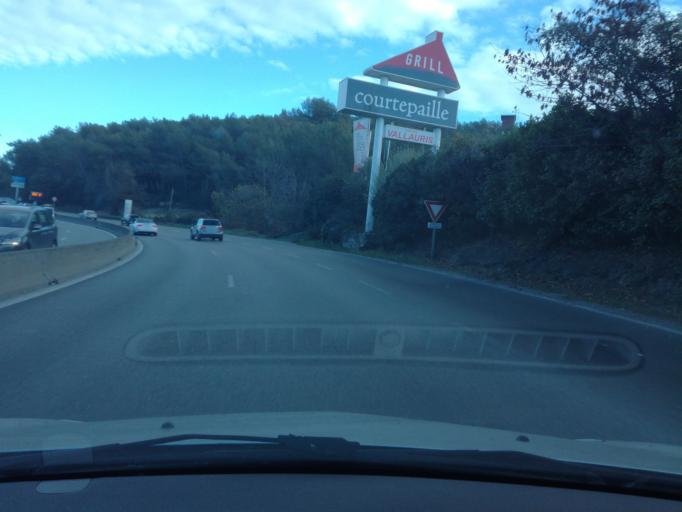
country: FR
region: Provence-Alpes-Cote d'Azur
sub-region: Departement des Alpes-Maritimes
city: Vallauris
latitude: 43.6032
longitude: 7.0638
